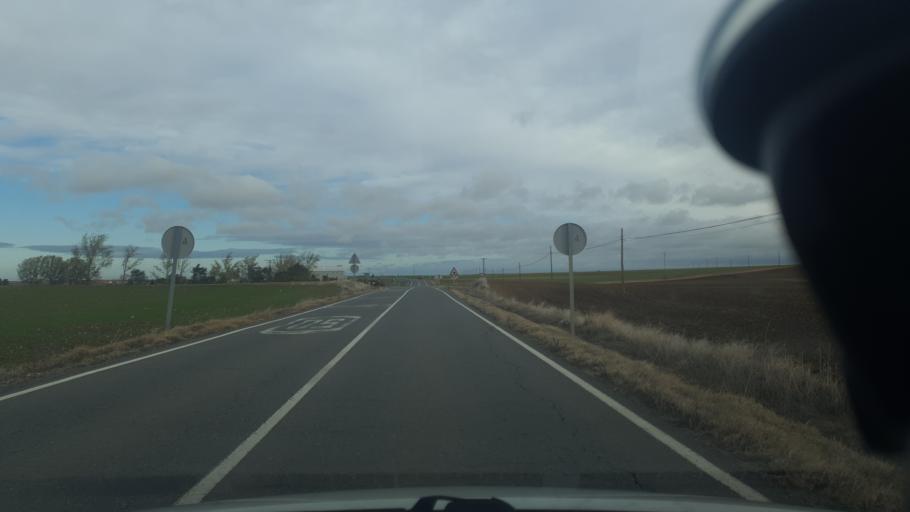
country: ES
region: Castille and Leon
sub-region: Provincia de Avila
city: Gotarrendura
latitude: 40.8039
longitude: -4.7589
